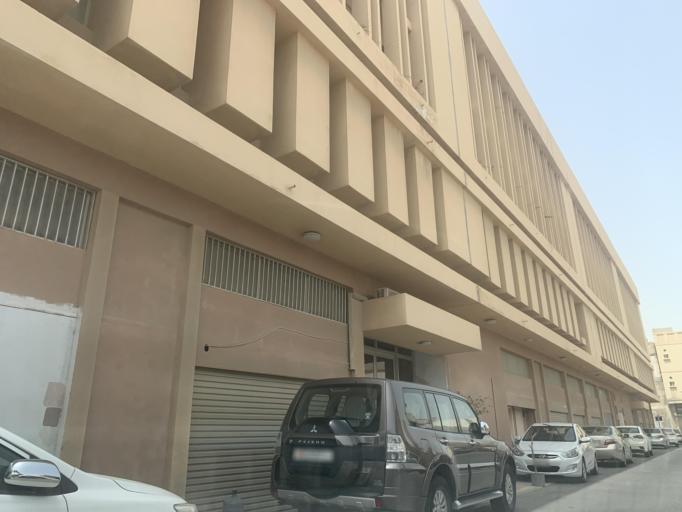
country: BH
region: Manama
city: Jidd Hafs
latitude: 26.2083
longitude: 50.5477
